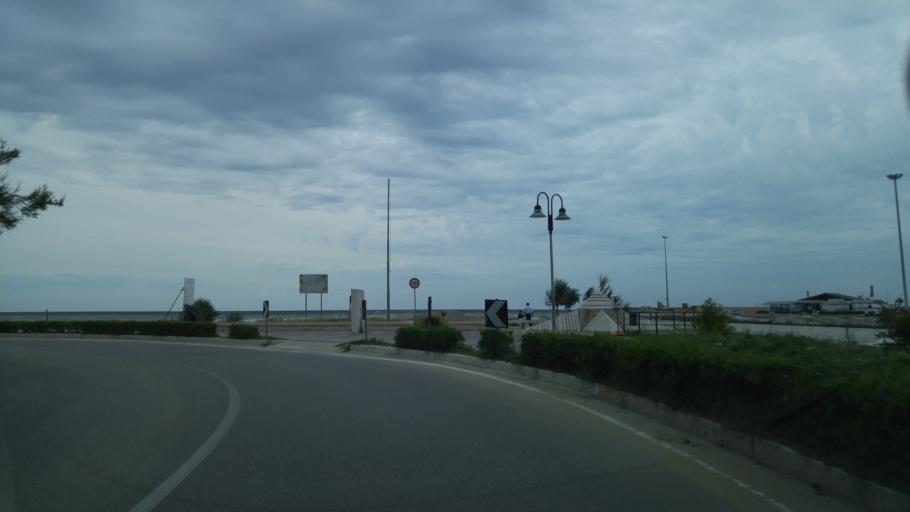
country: IT
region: The Marches
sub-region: Provincia di Pesaro e Urbino
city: Pesaro
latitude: 43.9222
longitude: 12.9018
